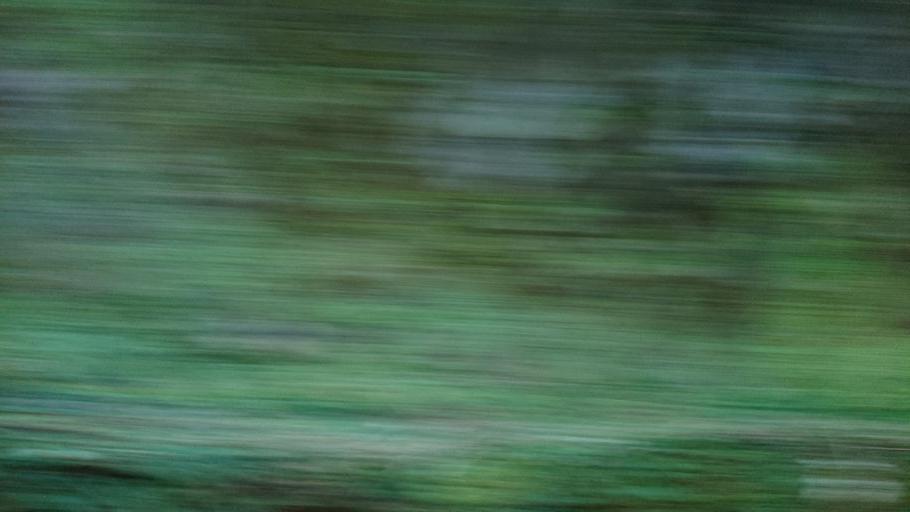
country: TW
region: Taiwan
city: Daxi
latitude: 24.4060
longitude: 121.3668
